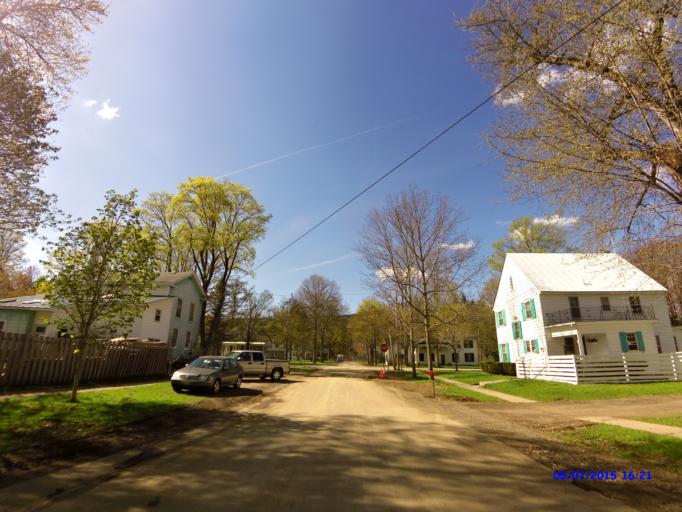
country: US
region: New York
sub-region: Cattaraugus County
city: Salamanca
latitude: 42.2740
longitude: -78.6740
